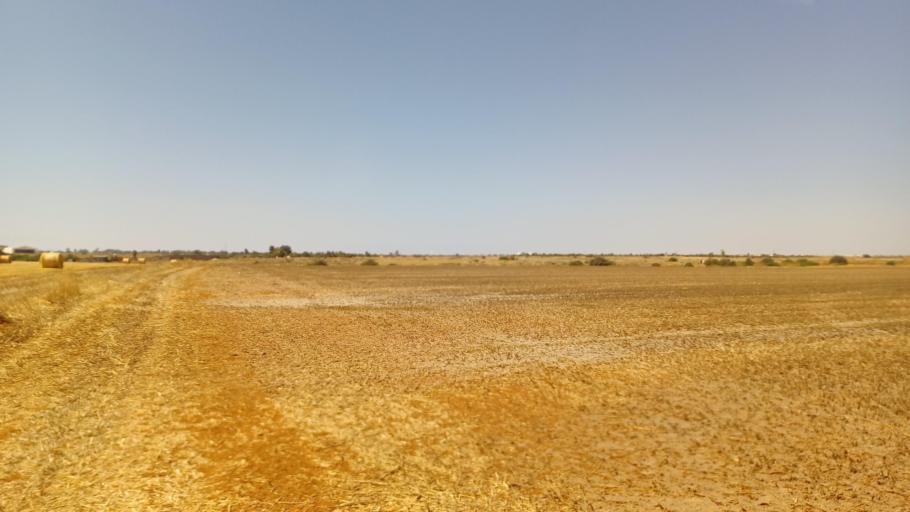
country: CY
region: Larnaka
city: Pergamos
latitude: 35.0253
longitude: 33.7209
